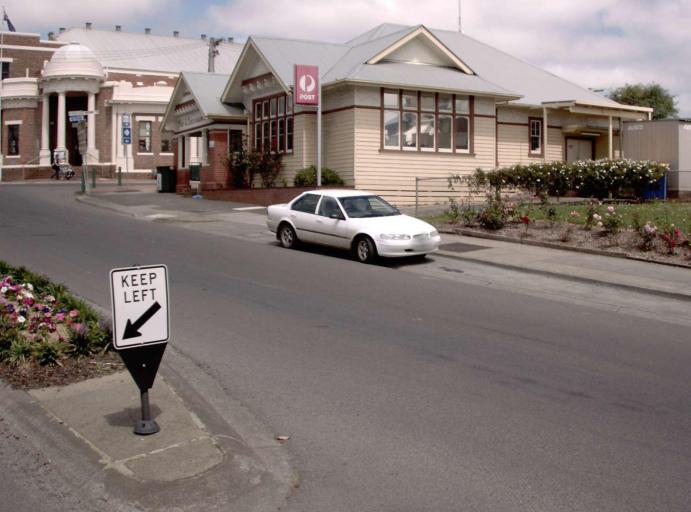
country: AU
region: Victoria
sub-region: Baw Baw
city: Warragul
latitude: -38.4763
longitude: 145.9466
